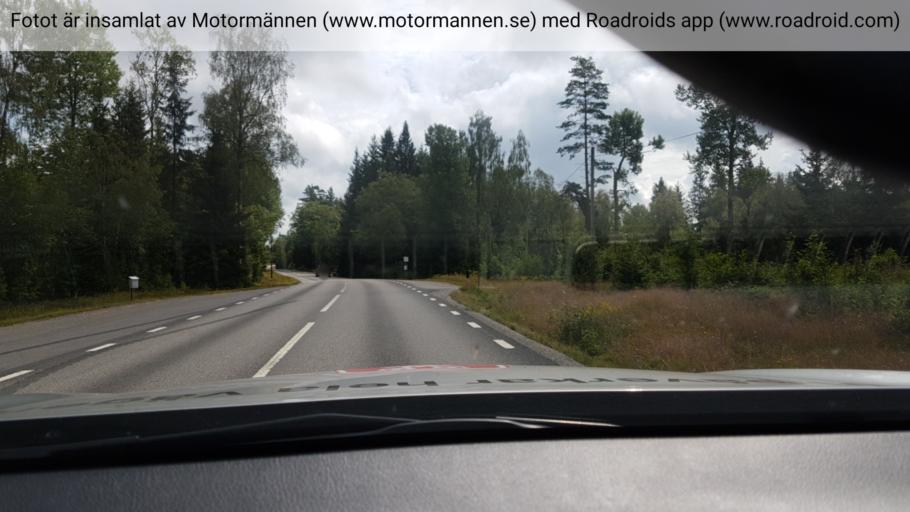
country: SE
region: Vaestra Goetaland
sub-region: Svenljunga Kommun
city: Svenljunga
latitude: 57.4826
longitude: 13.1465
